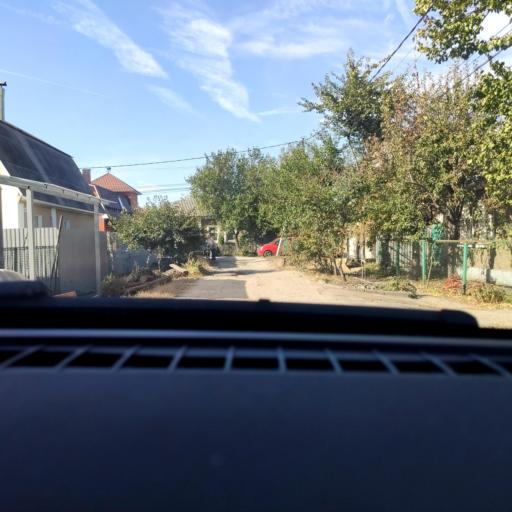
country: RU
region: Voronezj
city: Voronezh
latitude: 51.6732
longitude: 39.2668
